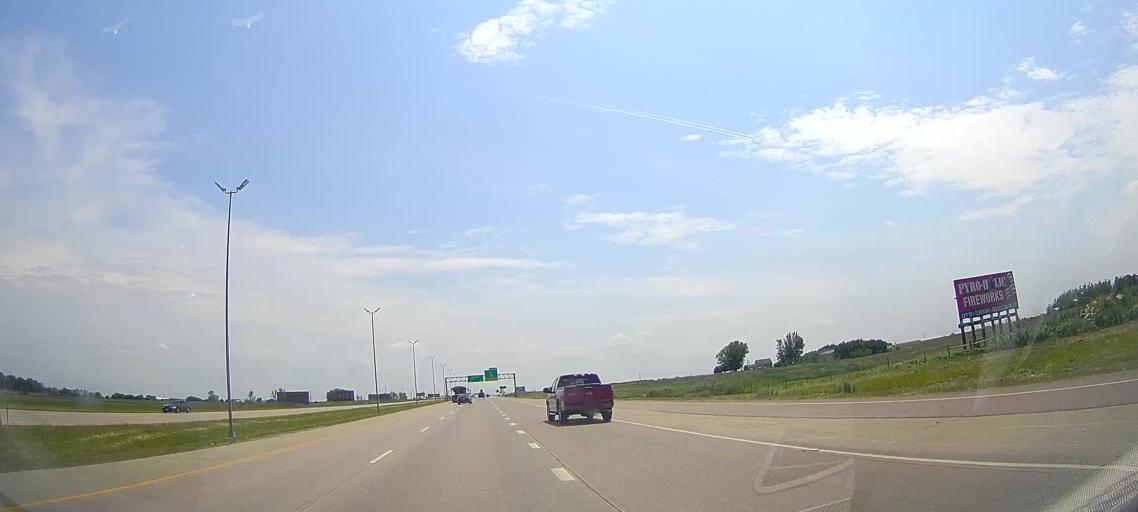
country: US
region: South Dakota
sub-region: Lincoln County
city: Tea
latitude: 43.4790
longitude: -96.7968
